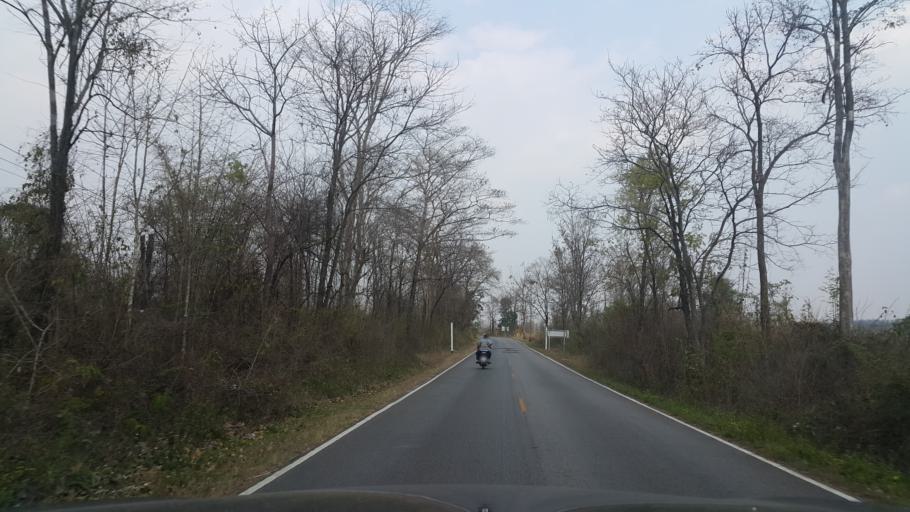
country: TH
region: Lamphun
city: Thung Hua Chang
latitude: 17.9613
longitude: 99.1540
